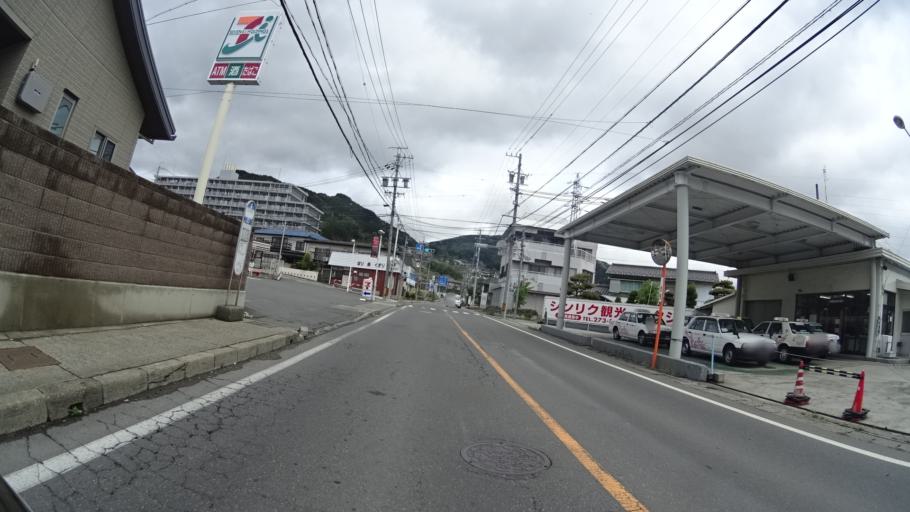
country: JP
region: Nagano
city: Nagano-shi
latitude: 36.6798
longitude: 138.2006
